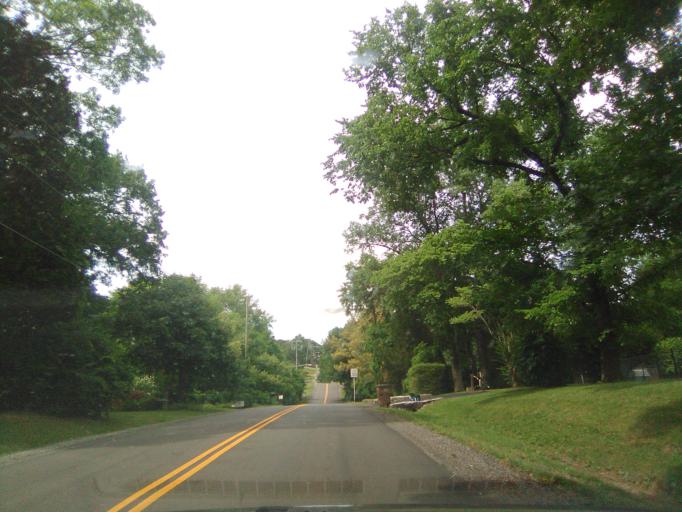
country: US
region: Tennessee
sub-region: Davidson County
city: Belle Meade
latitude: 36.1125
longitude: -86.8883
